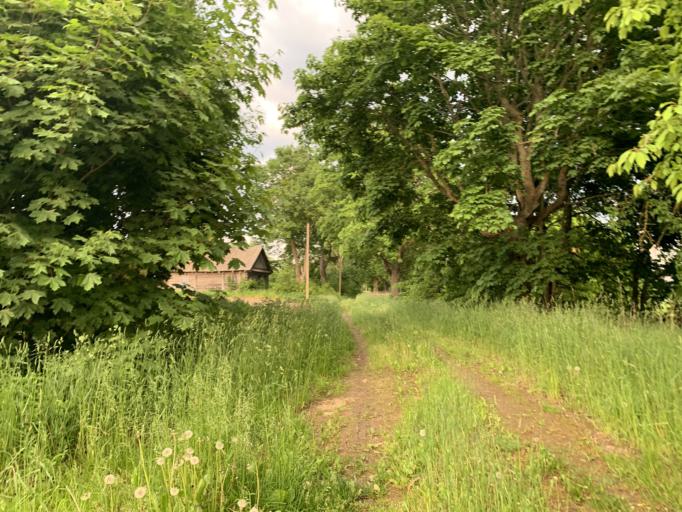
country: BY
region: Minsk
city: Nyasvizh
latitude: 53.1672
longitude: 26.8170
